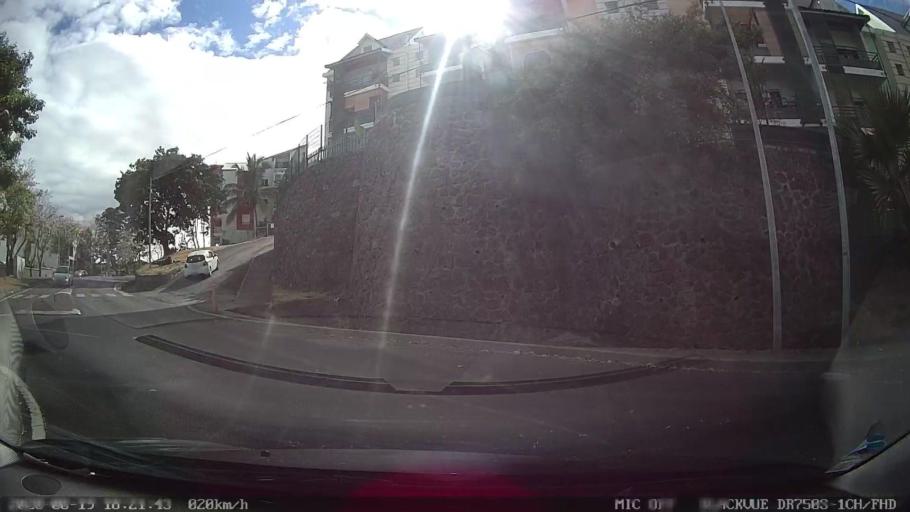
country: RE
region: Reunion
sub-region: Reunion
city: La Possession
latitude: -20.9574
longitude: 55.3364
